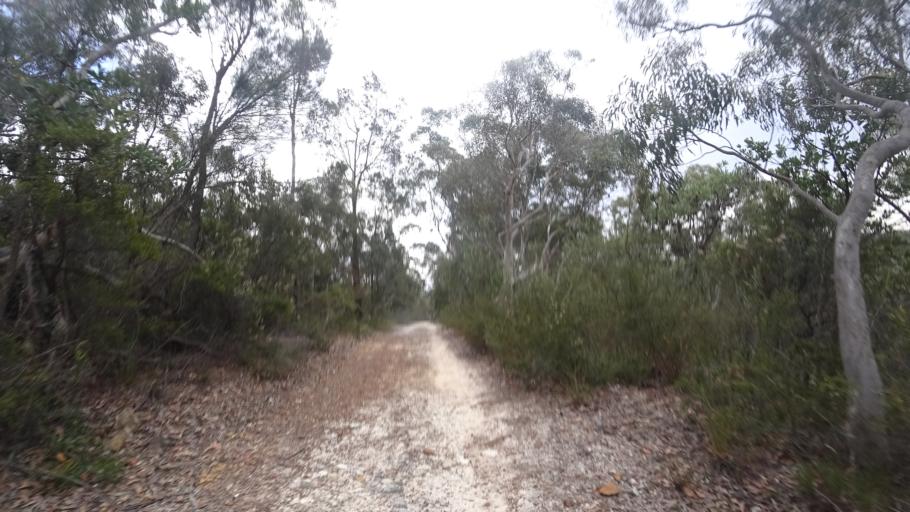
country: AU
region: New South Wales
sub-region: Warringah
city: Davidson
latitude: -33.6932
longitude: 151.1990
